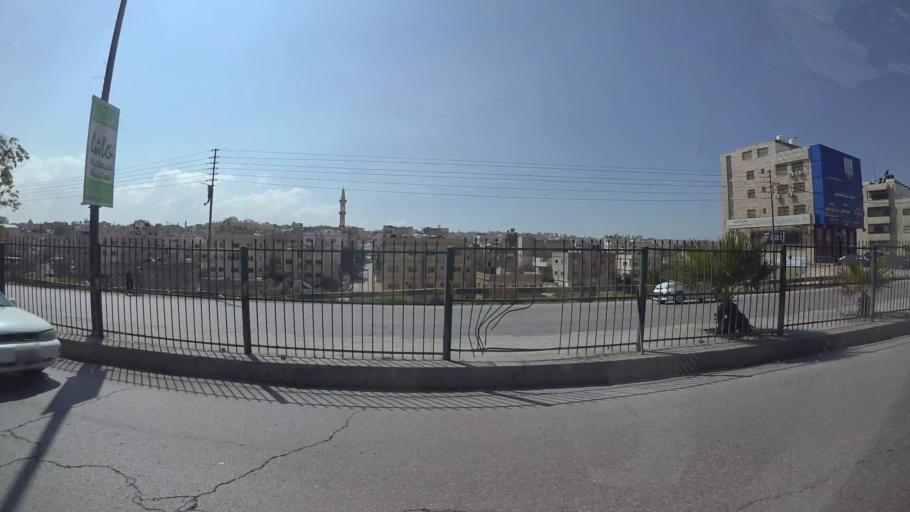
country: JO
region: Zarqa
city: Zarqa
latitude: 32.0438
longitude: 36.0941
